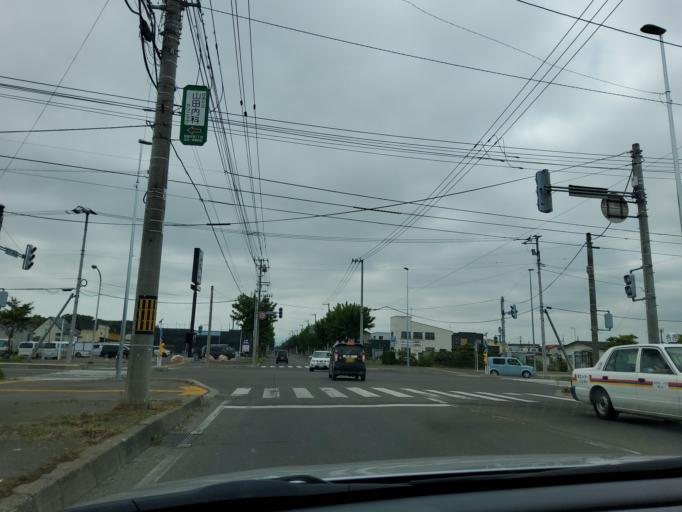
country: JP
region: Hokkaido
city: Obihiro
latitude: 42.9142
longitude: 143.1658
